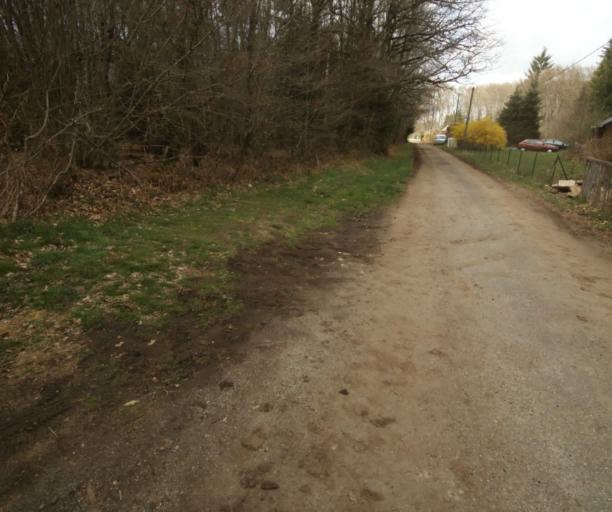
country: FR
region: Limousin
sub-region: Departement de la Correze
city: Correze
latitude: 45.2721
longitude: 1.9821
